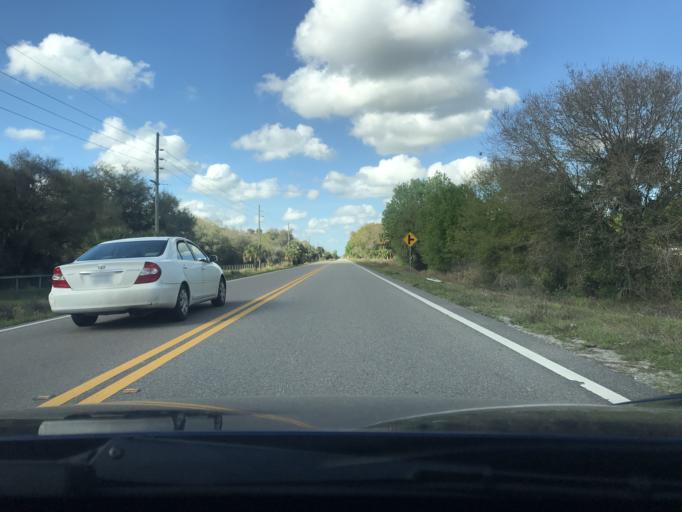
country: US
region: Florida
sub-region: Okeechobee County
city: Taylor Creek
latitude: 27.2012
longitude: -80.6940
